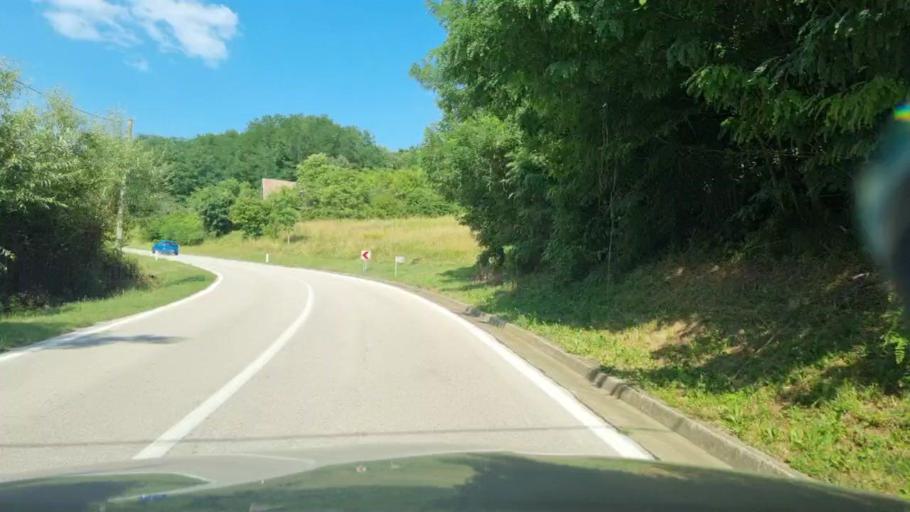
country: HR
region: Brodsko-Posavska
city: Garcin
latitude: 45.0937
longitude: 18.2229
